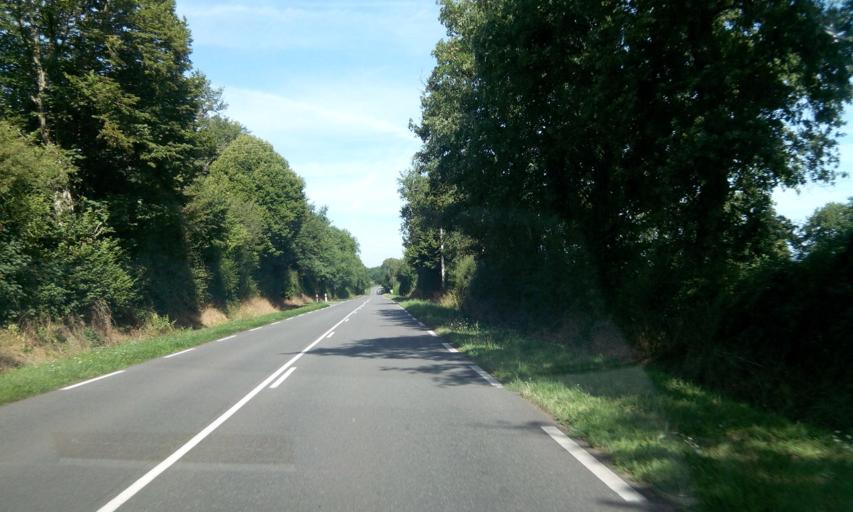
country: FR
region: Poitou-Charentes
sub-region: Departement de la Charente
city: Exideuil
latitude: 45.9506
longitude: 0.7157
